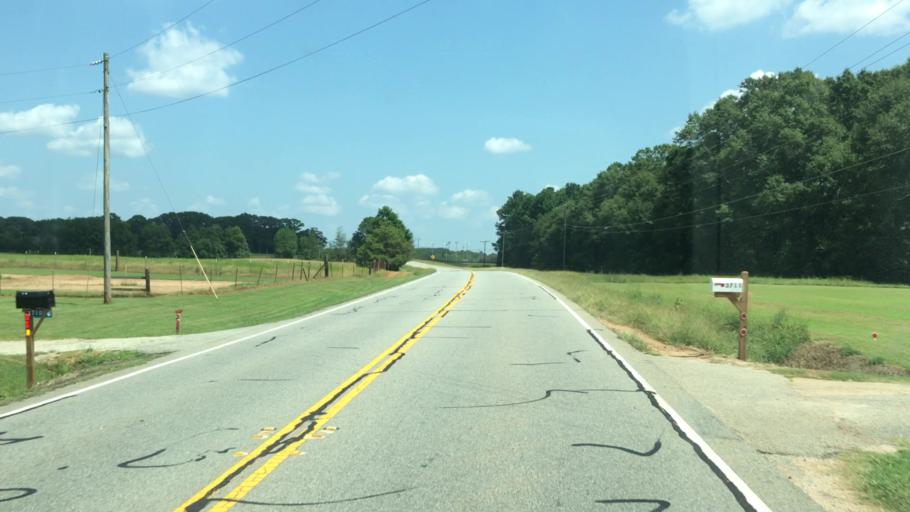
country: US
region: Georgia
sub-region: Oconee County
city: Watkinsville
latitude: 33.8673
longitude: -83.4870
